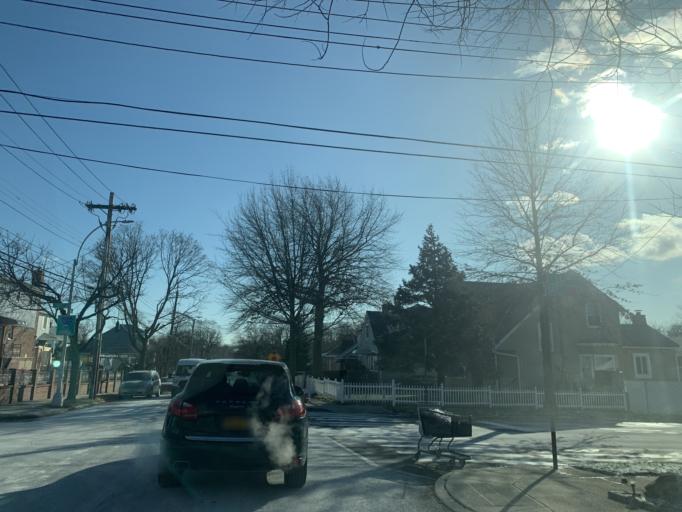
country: US
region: New York
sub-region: Nassau County
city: East Atlantic Beach
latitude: 40.7907
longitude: -73.8199
